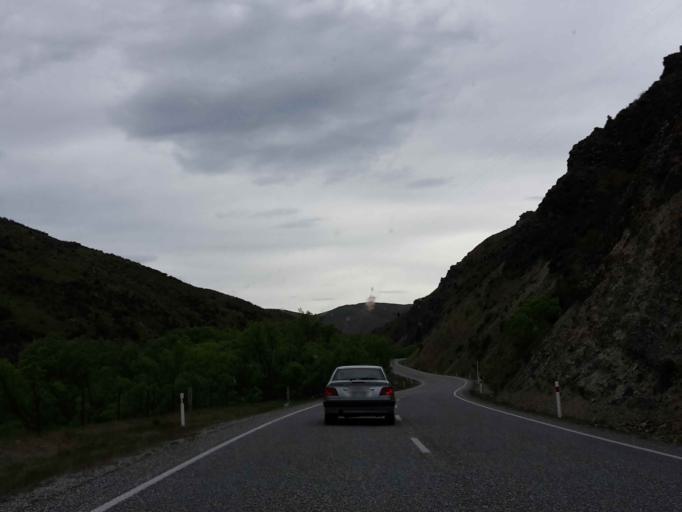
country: NZ
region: Otago
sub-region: Queenstown-Lakes District
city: Wanaka
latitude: -44.7288
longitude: 169.5065
